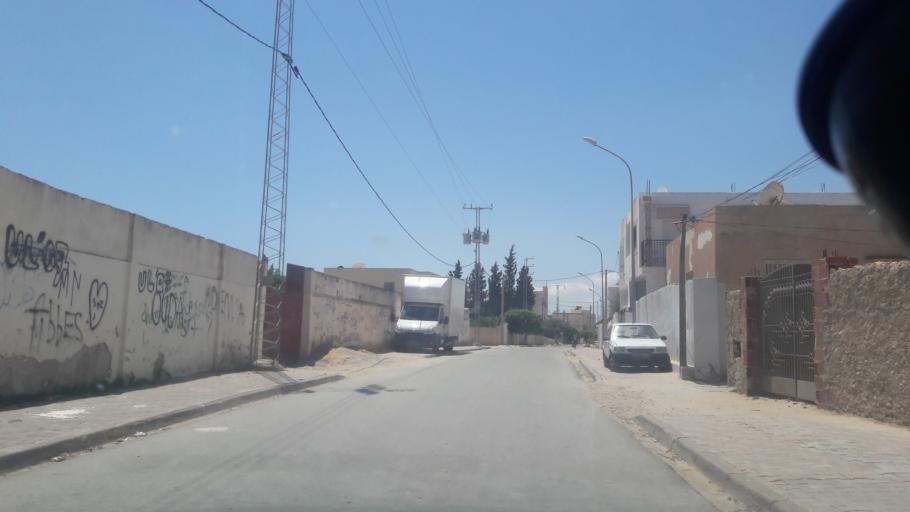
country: TN
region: Safaqis
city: Al Qarmadah
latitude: 34.8049
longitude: 10.7559
